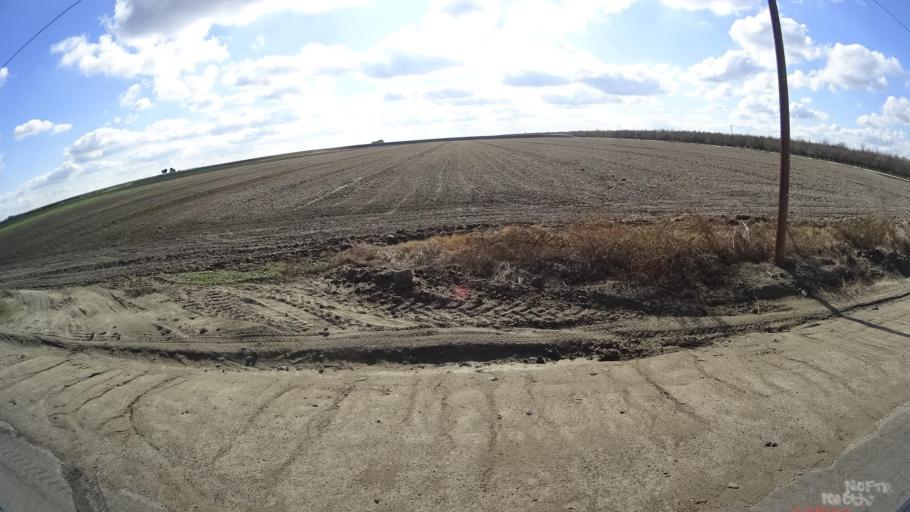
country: US
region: California
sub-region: Kern County
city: McFarland
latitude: 35.6887
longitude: -119.2841
